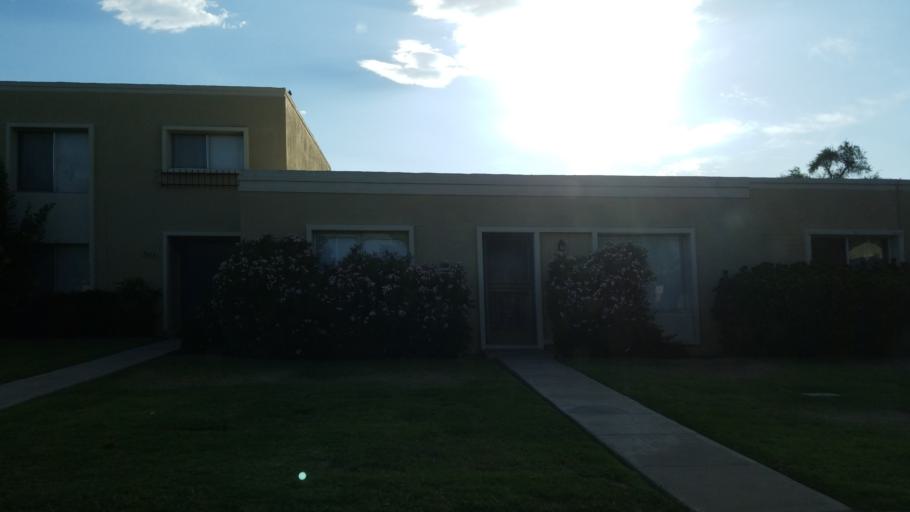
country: US
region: Arizona
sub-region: Maricopa County
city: Scottsdale
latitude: 33.5111
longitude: -111.9003
